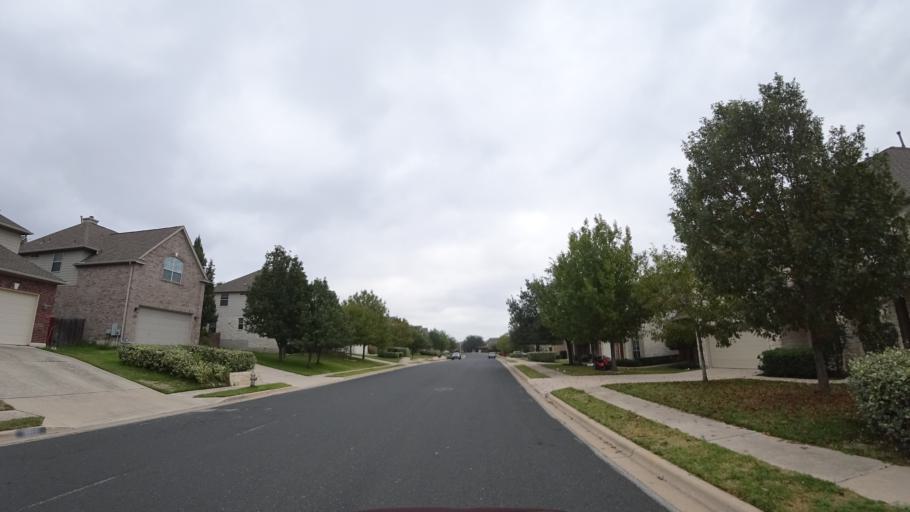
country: US
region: Texas
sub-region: Williamson County
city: Anderson Mill
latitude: 30.4337
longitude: -97.8217
